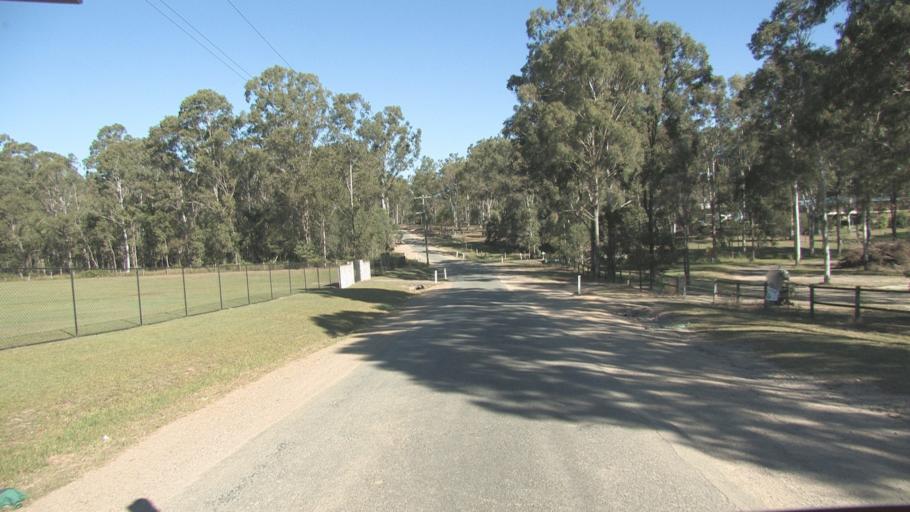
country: AU
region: Queensland
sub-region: Logan
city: Windaroo
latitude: -27.7572
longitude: 153.1510
